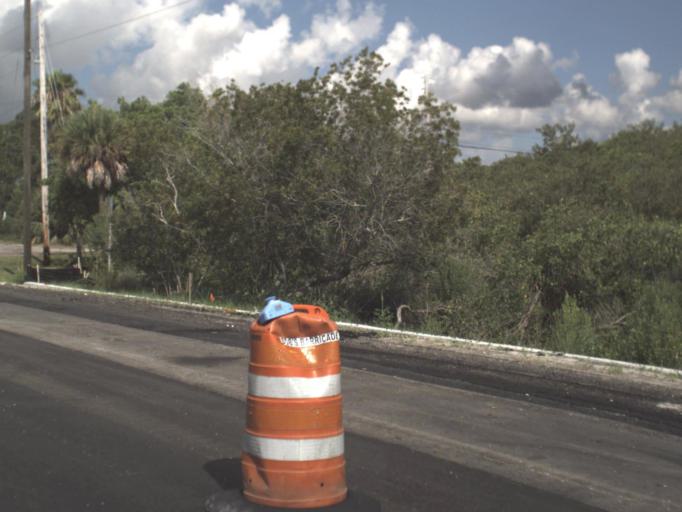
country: US
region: Florida
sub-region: Pinellas County
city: Safety Harbor
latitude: 27.9612
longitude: -82.6976
